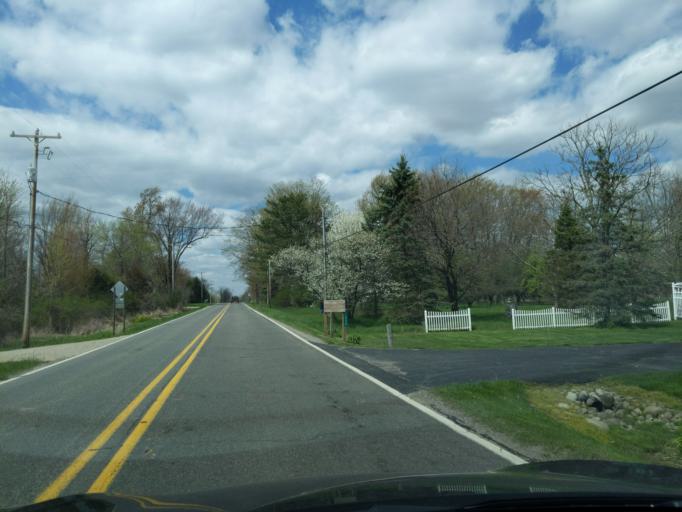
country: US
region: Michigan
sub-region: Ingham County
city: Mason
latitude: 42.6126
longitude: -84.4574
